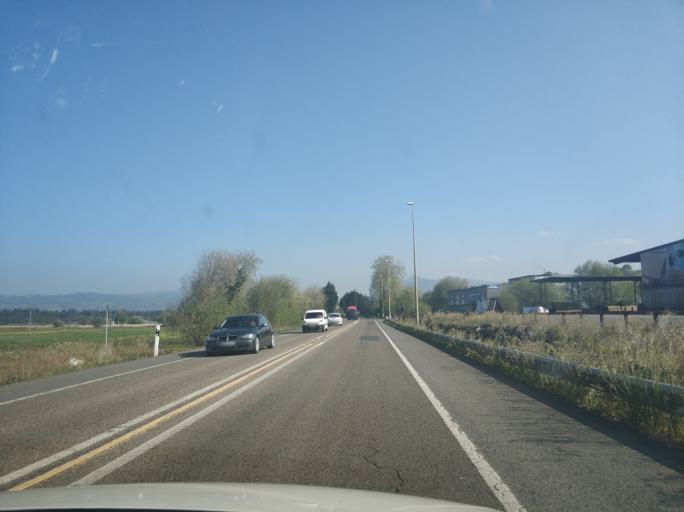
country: ES
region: Cantabria
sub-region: Provincia de Cantabria
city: Barcena de Cicero
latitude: 43.4079
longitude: -3.4838
